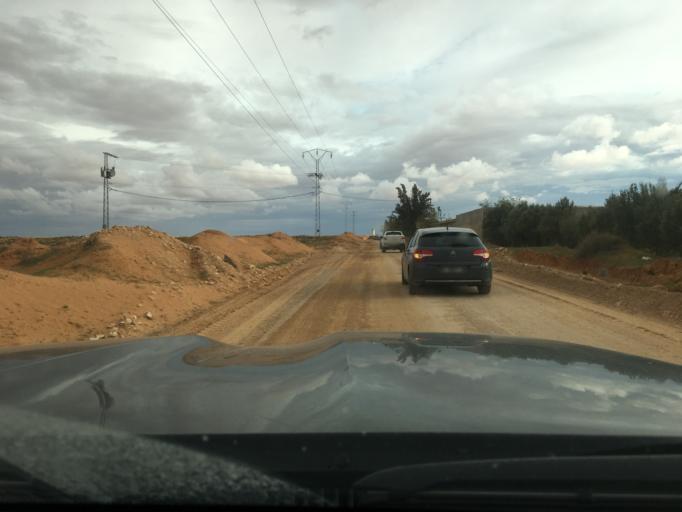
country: TN
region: Madanin
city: Medenine
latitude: 33.2747
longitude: 10.5629
